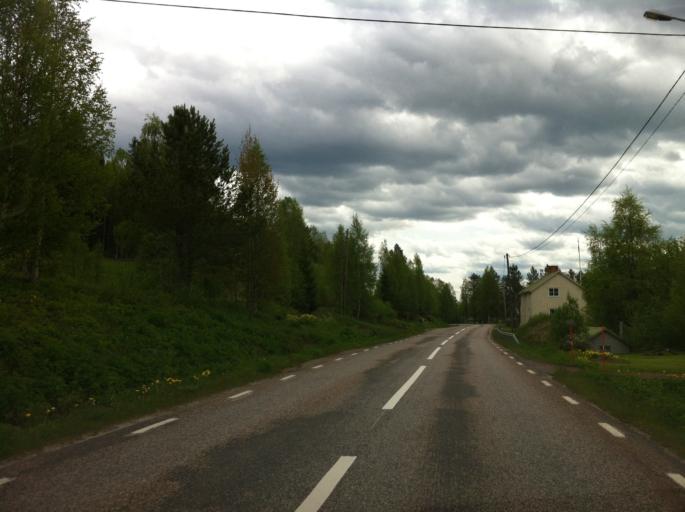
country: SE
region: Dalarna
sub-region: Malung-Saelens kommun
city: Malung
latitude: 61.2065
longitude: 13.2248
